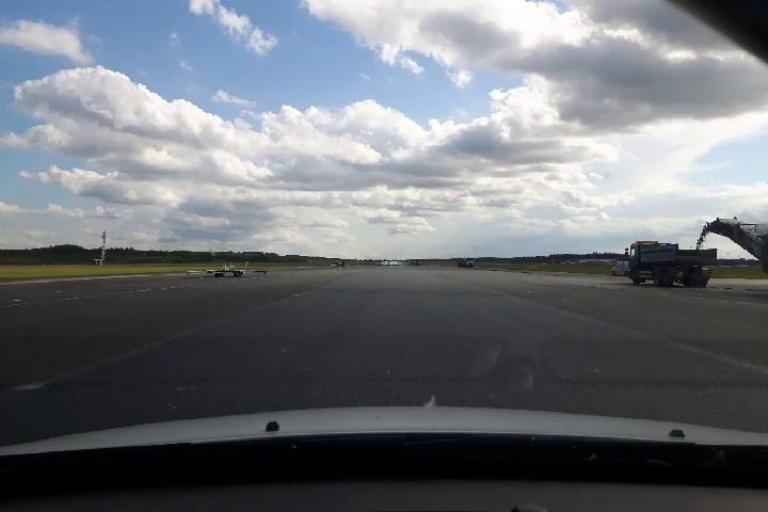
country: SE
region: Stockholm
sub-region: Sigtuna Kommun
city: Rosersberg
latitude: 59.6472
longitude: 17.9582
